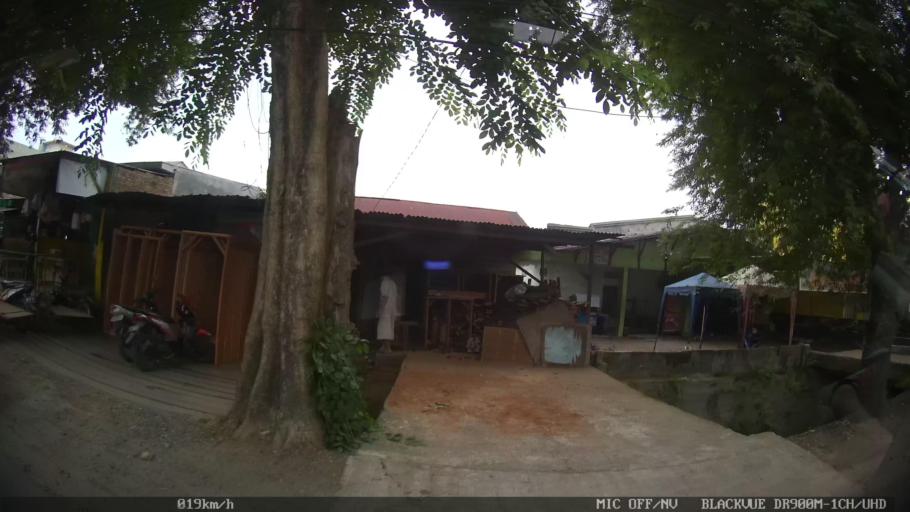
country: ID
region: North Sumatra
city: Deli Tua
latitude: 3.5521
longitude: 98.7121
